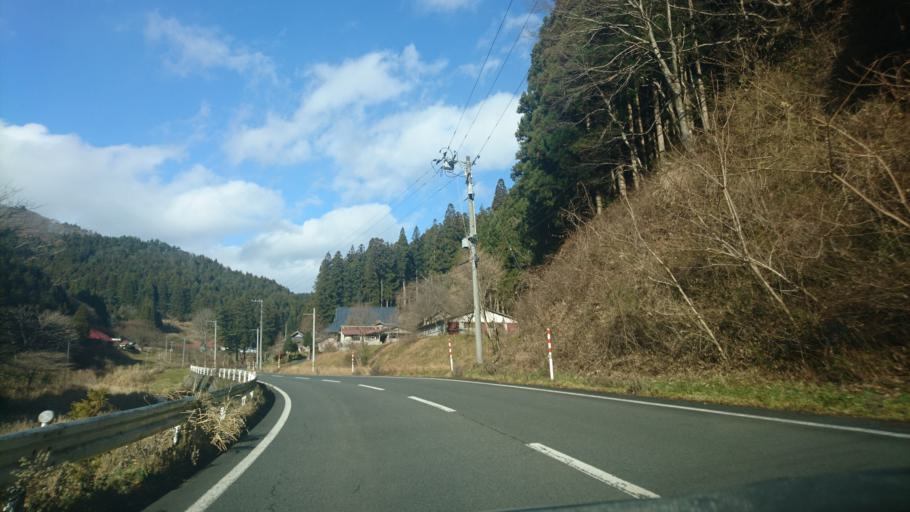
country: JP
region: Iwate
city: Mizusawa
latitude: 39.0904
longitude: 141.3862
